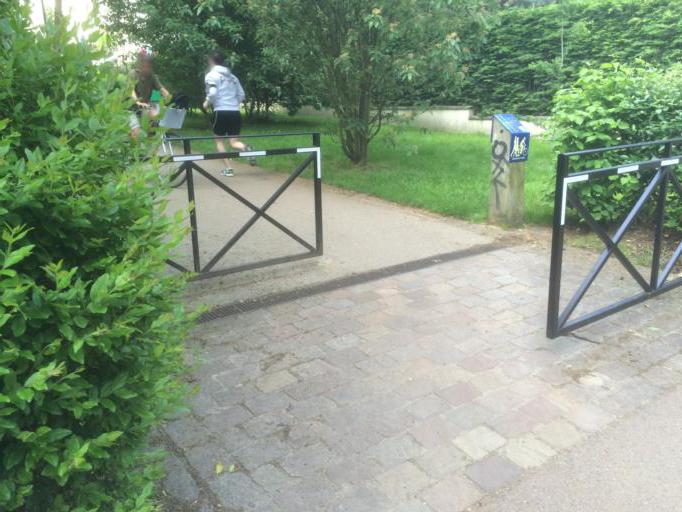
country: FR
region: Ile-de-France
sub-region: Departement des Hauts-de-Seine
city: Sceaux
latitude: 48.7803
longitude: 2.2866
